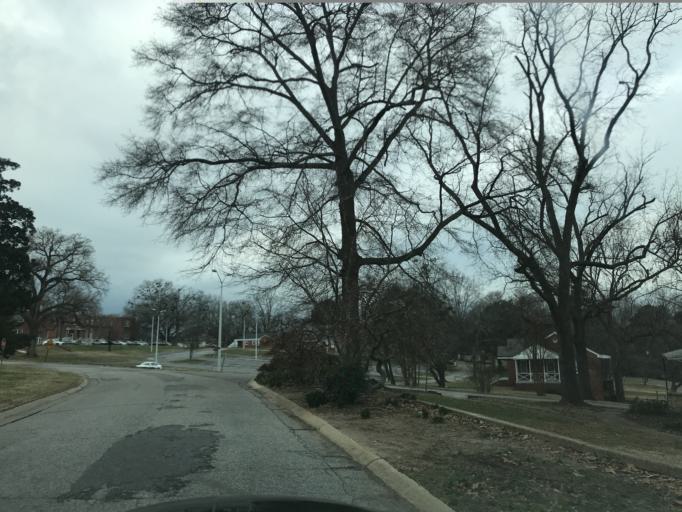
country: US
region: North Carolina
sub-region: Wake County
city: Raleigh
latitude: 35.7703
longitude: -78.6550
